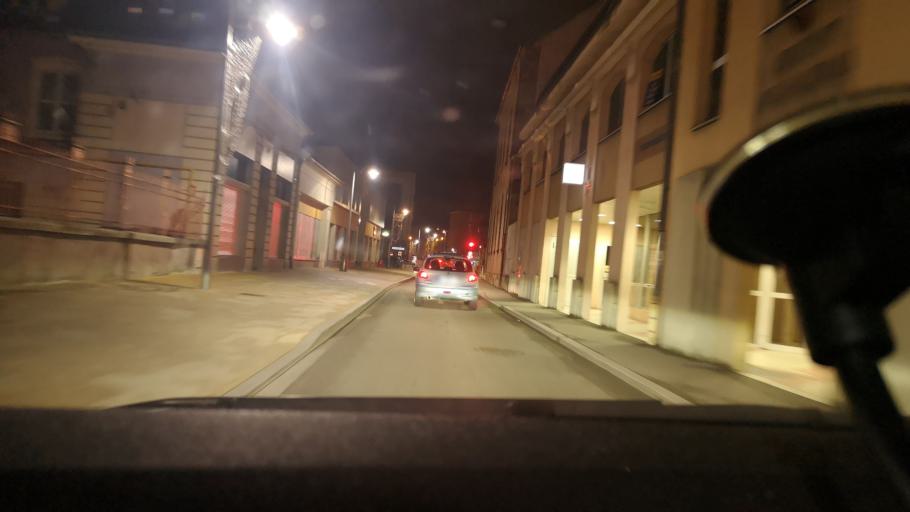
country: FR
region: Franche-Comte
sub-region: Territoire de Belfort
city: Belfort
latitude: 47.6379
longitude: 6.8573
